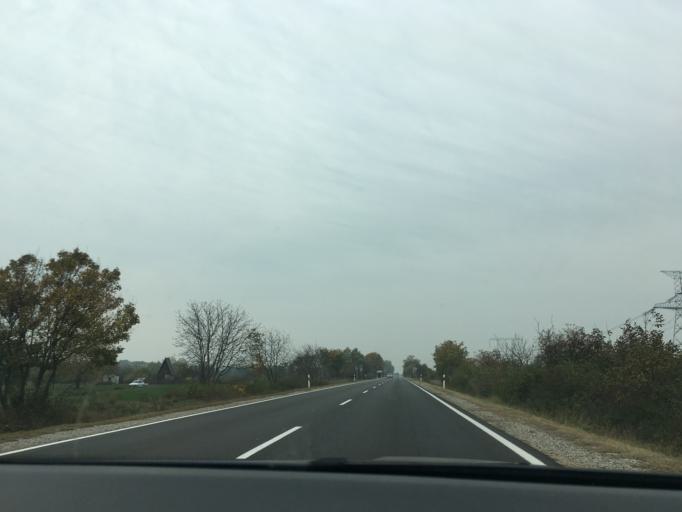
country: HU
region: Hajdu-Bihar
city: Puspokladany
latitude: 47.3309
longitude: 21.1045
